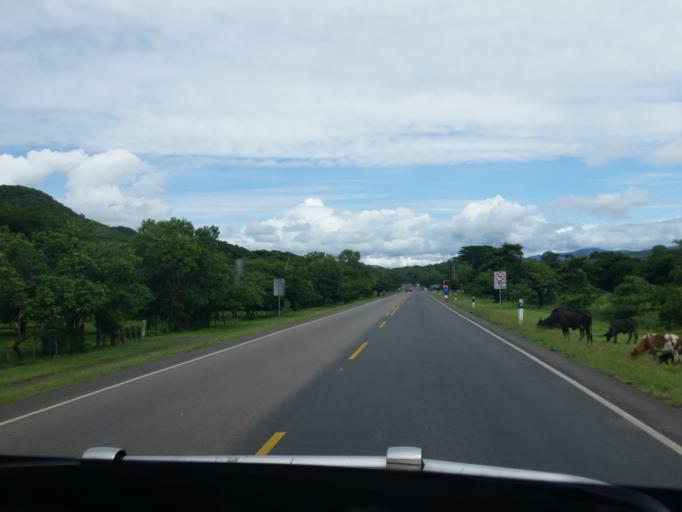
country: NI
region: Matagalpa
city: Ciudad Dario
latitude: 12.5981
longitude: -86.0454
